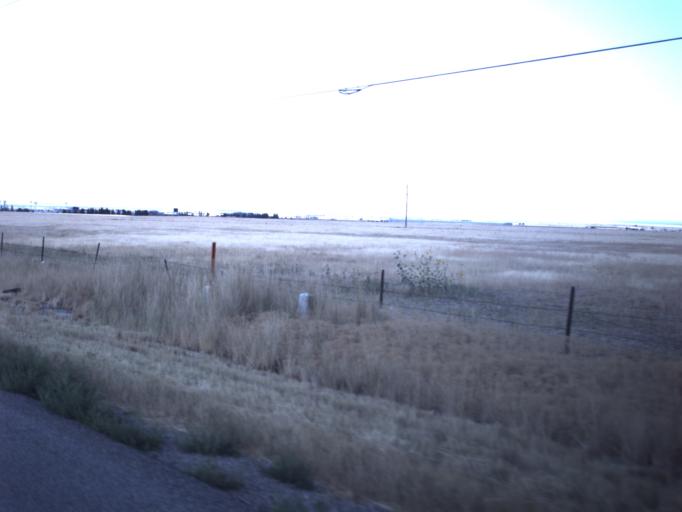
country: US
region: Utah
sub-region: Tooele County
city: Tooele
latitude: 40.5630
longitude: -112.3584
